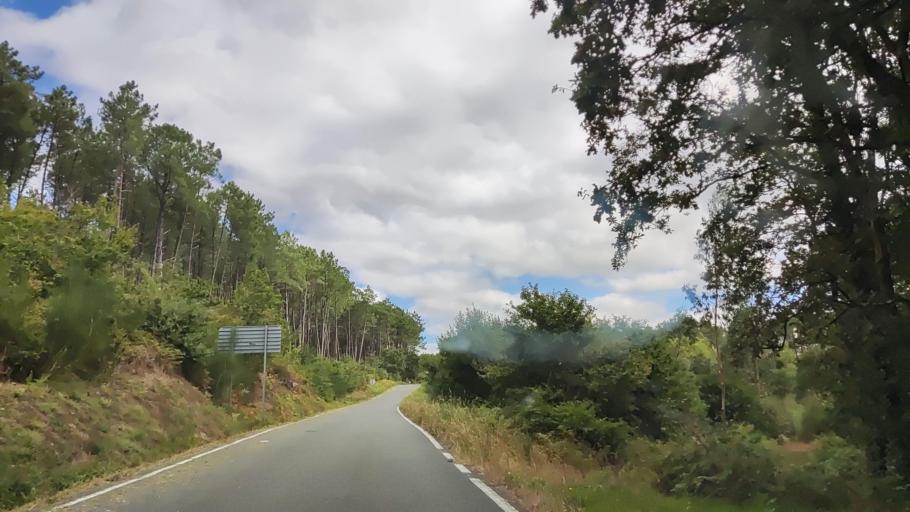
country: ES
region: Galicia
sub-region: Provincia da Coruna
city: Rois
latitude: 42.7309
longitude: -8.7071
